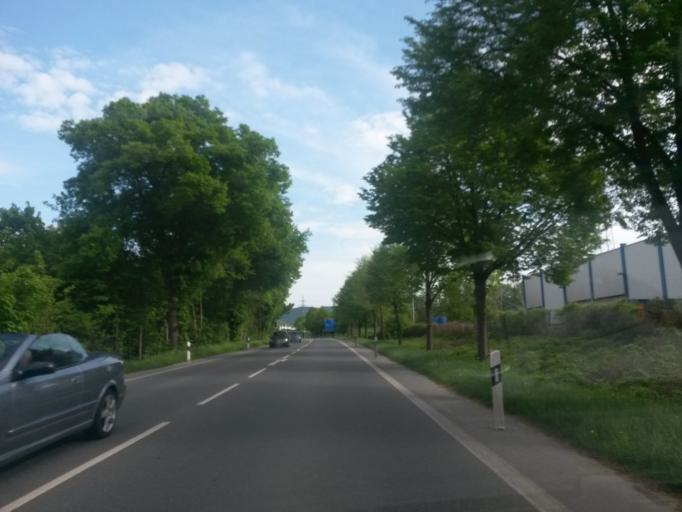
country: DE
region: North Rhine-Westphalia
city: Schwerte
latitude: 51.3728
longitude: 7.5459
